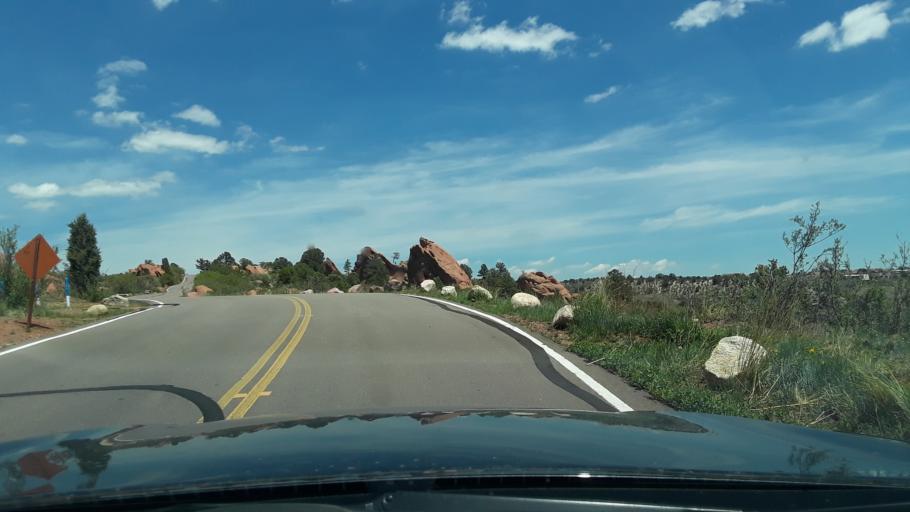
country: US
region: Colorado
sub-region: El Paso County
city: Manitou Springs
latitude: 38.8616
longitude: -104.8791
